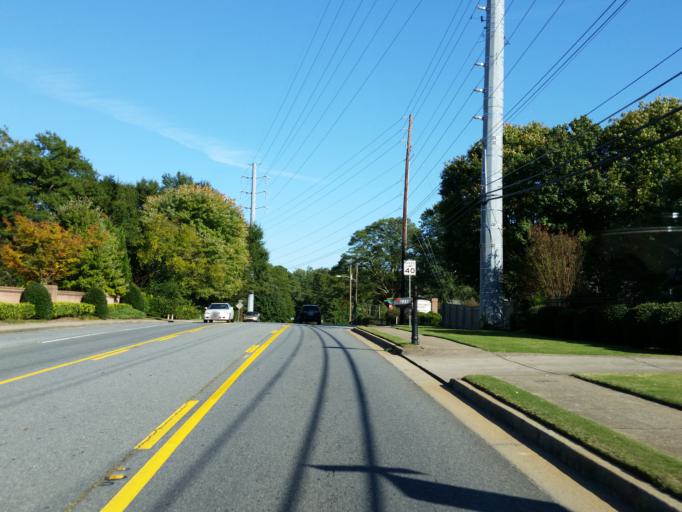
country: US
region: Georgia
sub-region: Cobb County
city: Marietta
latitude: 34.0159
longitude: -84.4860
